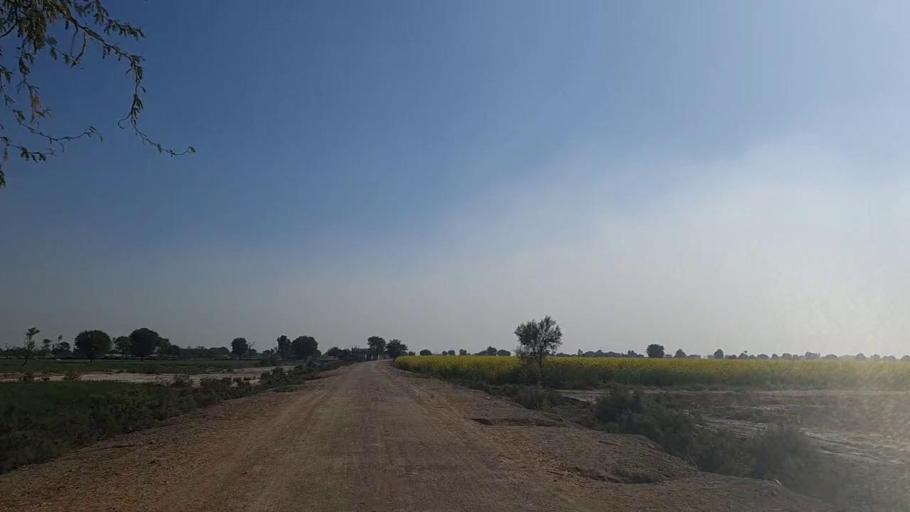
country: PK
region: Sindh
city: Shahpur Chakar
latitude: 26.2048
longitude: 68.6124
